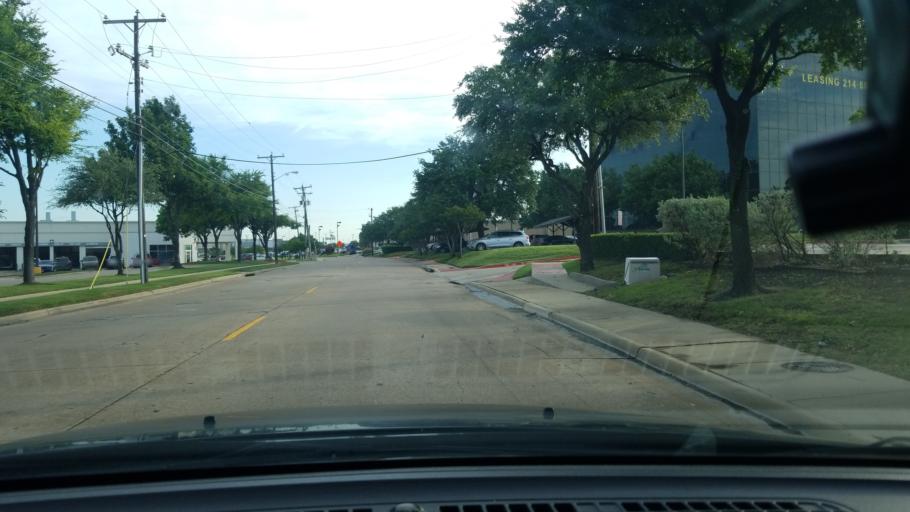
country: US
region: Texas
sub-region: Dallas County
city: Mesquite
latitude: 32.8024
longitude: -96.6288
